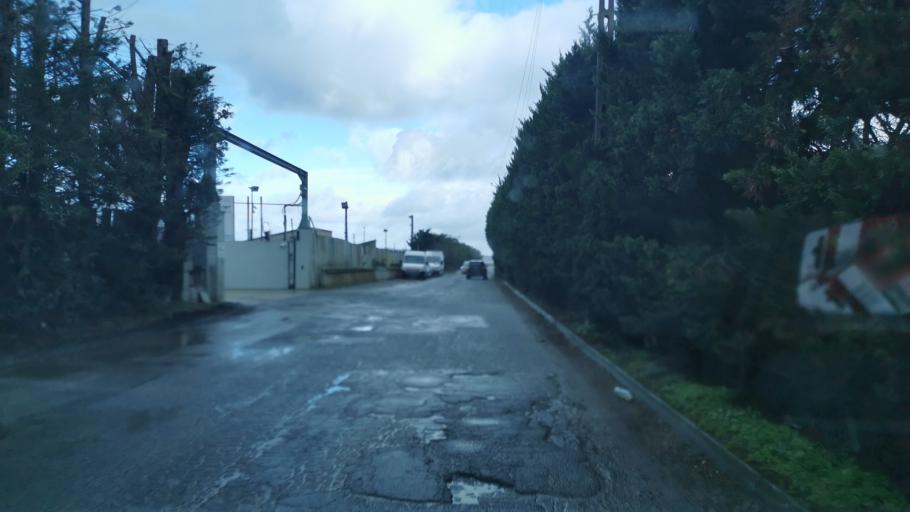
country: FR
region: Ile-de-France
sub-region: Departement de l'Essonne
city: Boissy-sous-Saint-Yon
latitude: 48.5608
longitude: 2.2242
